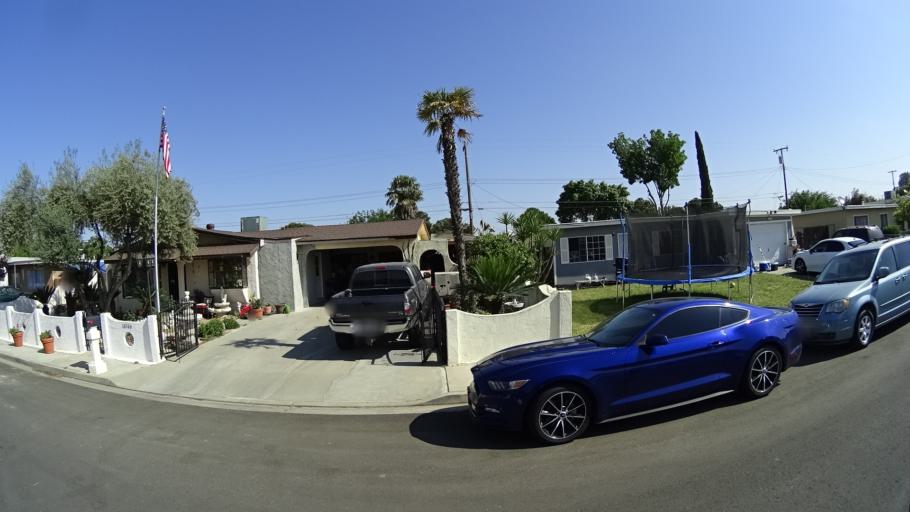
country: US
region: California
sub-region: Kings County
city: Home Garden
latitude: 36.3003
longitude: -119.6389
